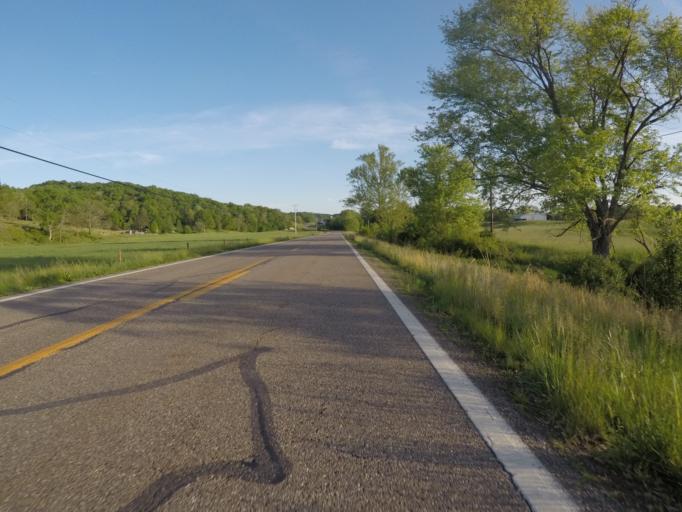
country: US
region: West Virginia
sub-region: Cabell County
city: Huntington
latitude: 38.5396
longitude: -82.4608
